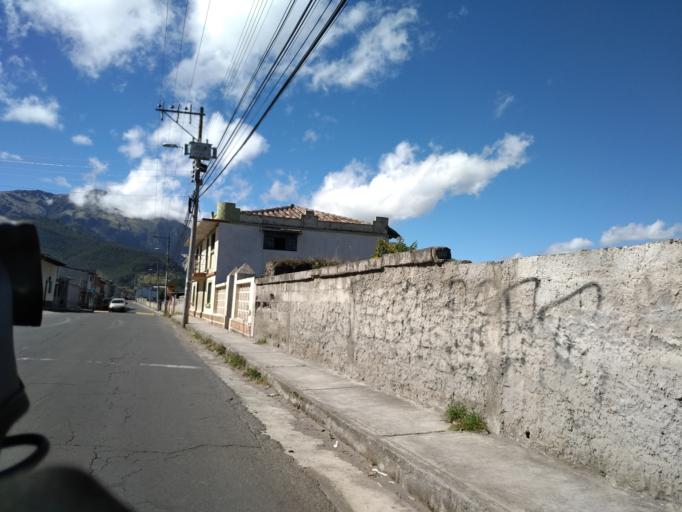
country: EC
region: Imbabura
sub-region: Canton Otavalo
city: Otavalo
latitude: 0.2012
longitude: -78.1950
